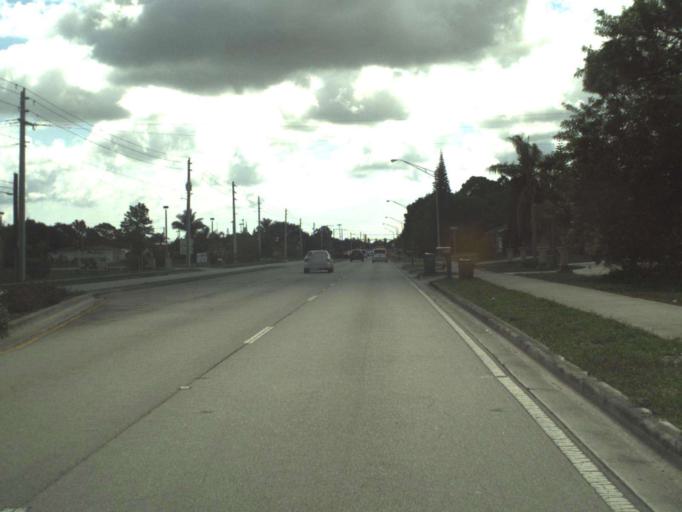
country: US
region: Florida
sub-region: Saint Lucie County
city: River Park
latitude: 27.3177
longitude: -80.3583
